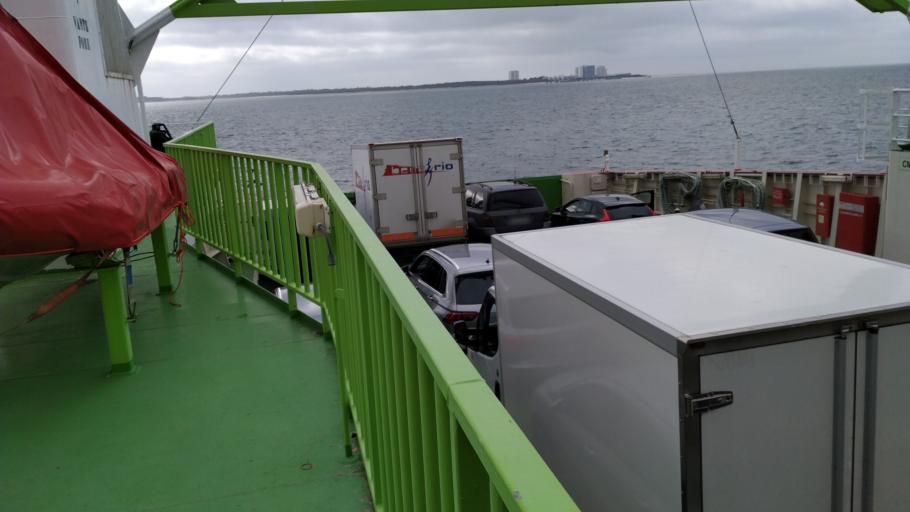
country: PT
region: Setubal
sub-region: Setubal
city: Setubal
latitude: 38.5182
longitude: -8.8857
